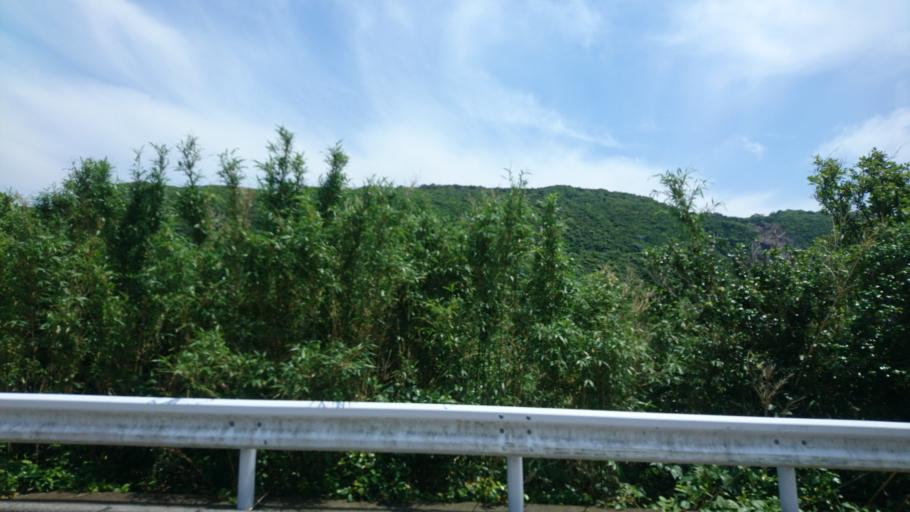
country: JP
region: Shizuoka
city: Shimoda
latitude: 34.4112
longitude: 139.2802
